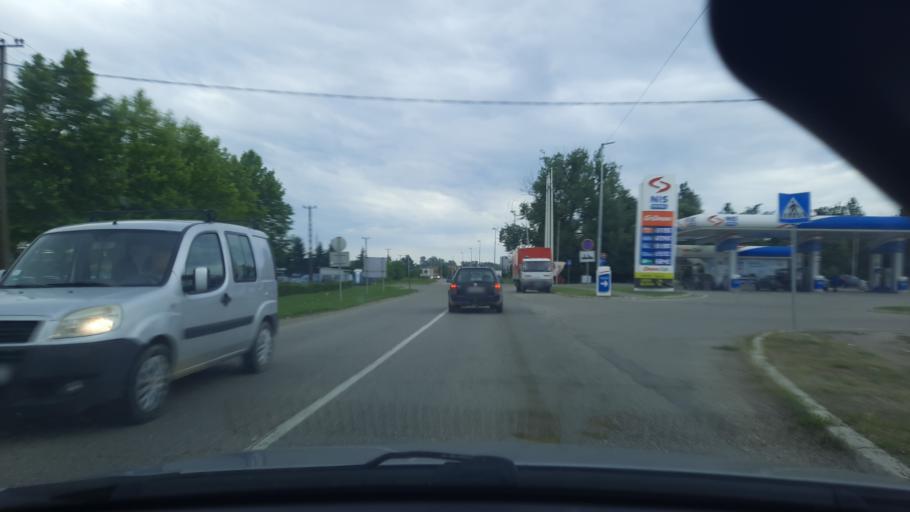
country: RS
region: Central Serbia
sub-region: Macvanski Okrug
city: Sabac
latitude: 44.7395
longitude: 19.6748
